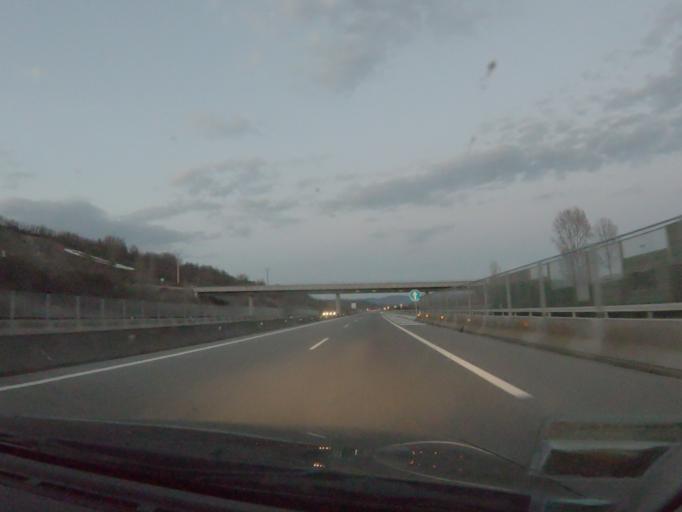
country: ES
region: Castille and Leon
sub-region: Provincia de Leon
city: Congosto
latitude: 42.5994
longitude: -6.5020
